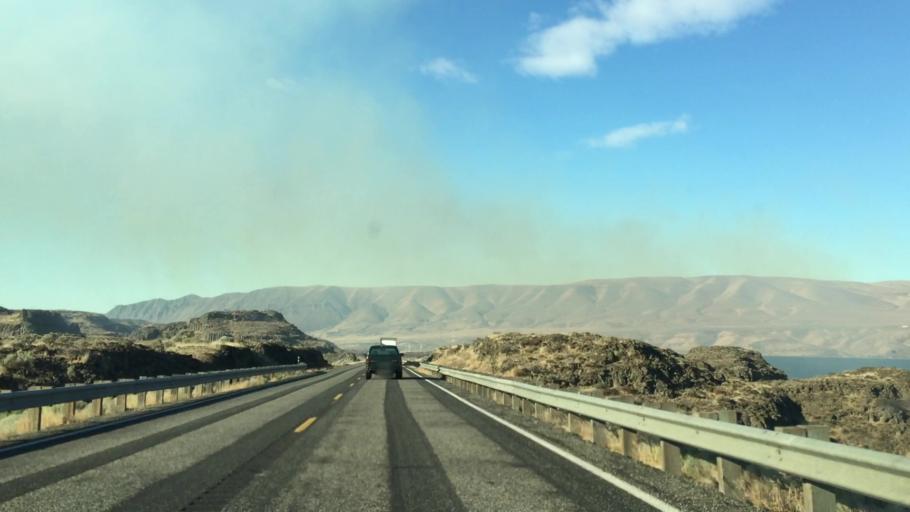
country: US
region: Washington
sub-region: Grant County
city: Mattawa
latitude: 46.9050
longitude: -119.9489
